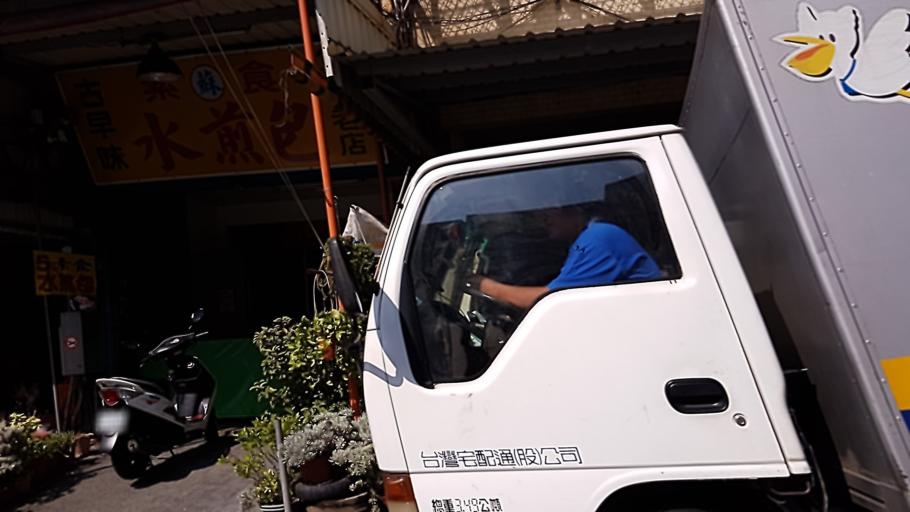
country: TW
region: Taiwan
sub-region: Changhua
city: Chang-hua
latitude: 24.0837
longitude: 120.4773
